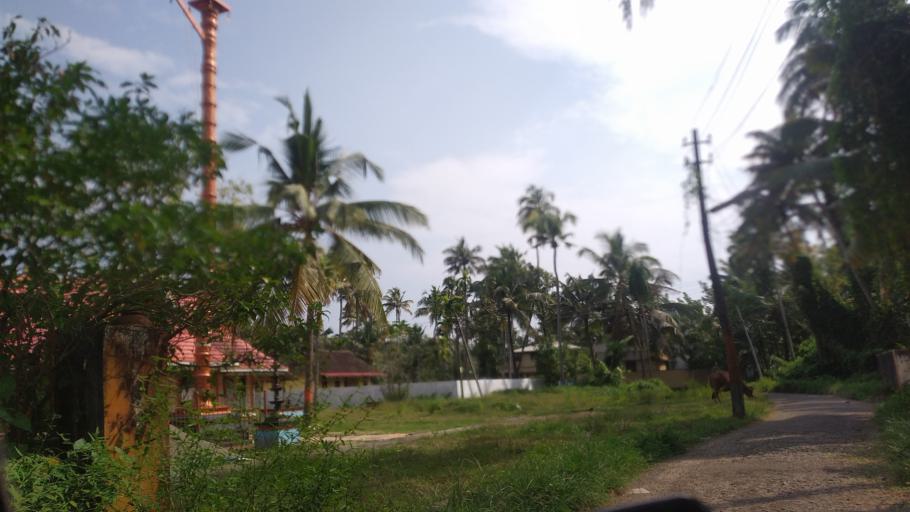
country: IN
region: Kerala
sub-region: Ernakulam
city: Elur
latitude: 10.0821
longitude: 76.2198
